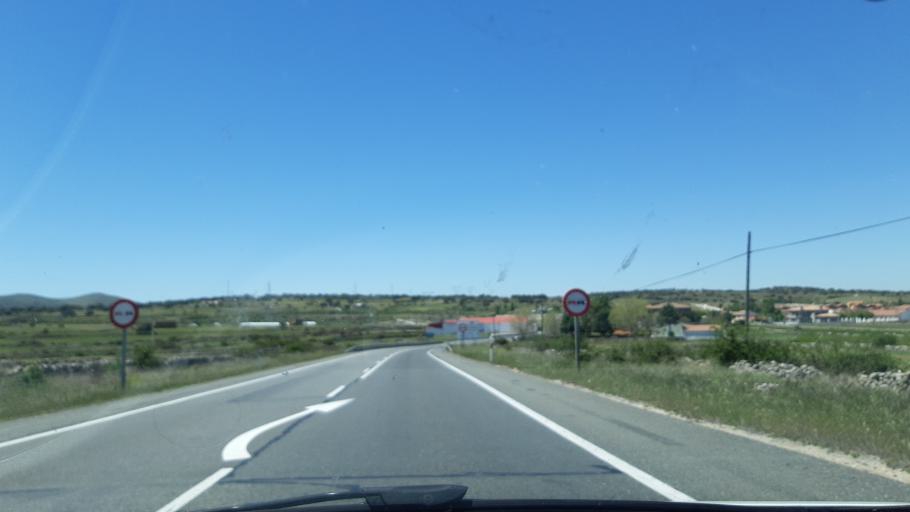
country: ES
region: Castille and Leon
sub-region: Provincia de Segovia
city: Zarzuela del Monte
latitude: 40.7556
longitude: -4.3255
